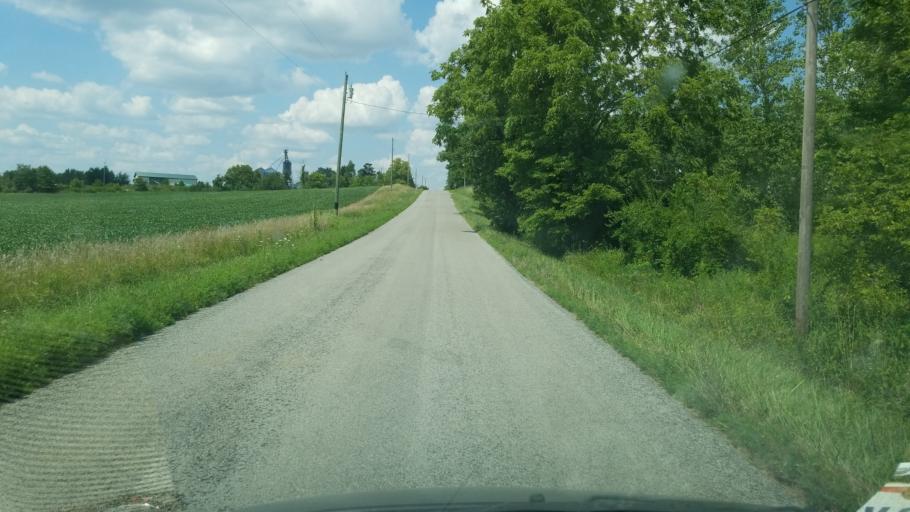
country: US
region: Ohio
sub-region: Champaign County
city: North Lewisburg
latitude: 40.2234
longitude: -83.4946
